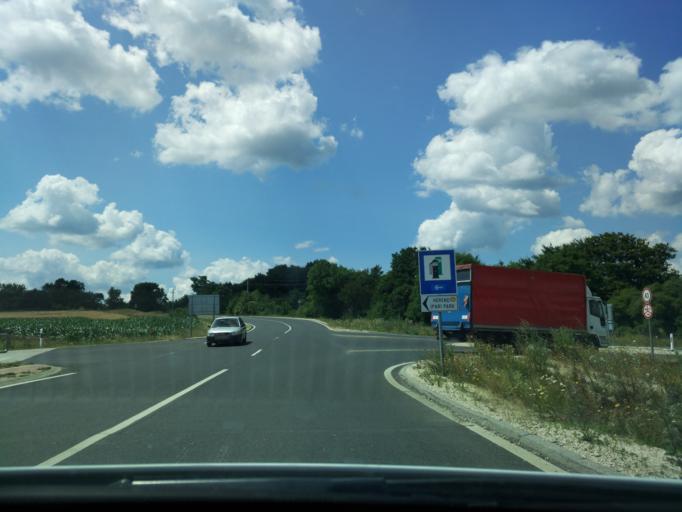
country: HU
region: Veszprem
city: Herend
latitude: 47.1294
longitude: 17.7479
